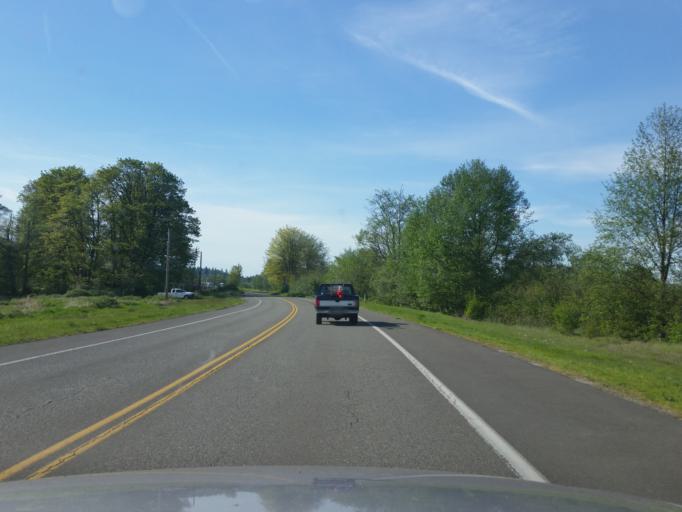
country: US
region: Washington
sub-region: Snohomish County
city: Everett
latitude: 47.9413
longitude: -122.1728
